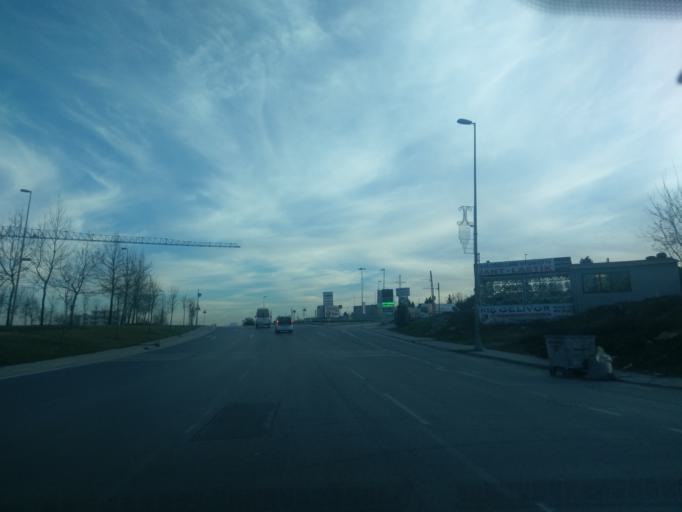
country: TR
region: Istanbul
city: Basaksehir
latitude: 41.0425
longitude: 28.7593
